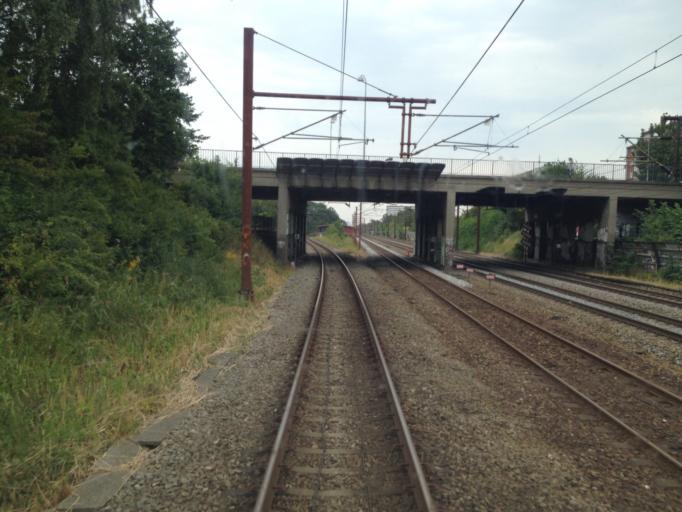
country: DK
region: Capital Region
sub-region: Rodovre Kommune
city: Rodovre
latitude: 55.6651
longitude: 12.4366
